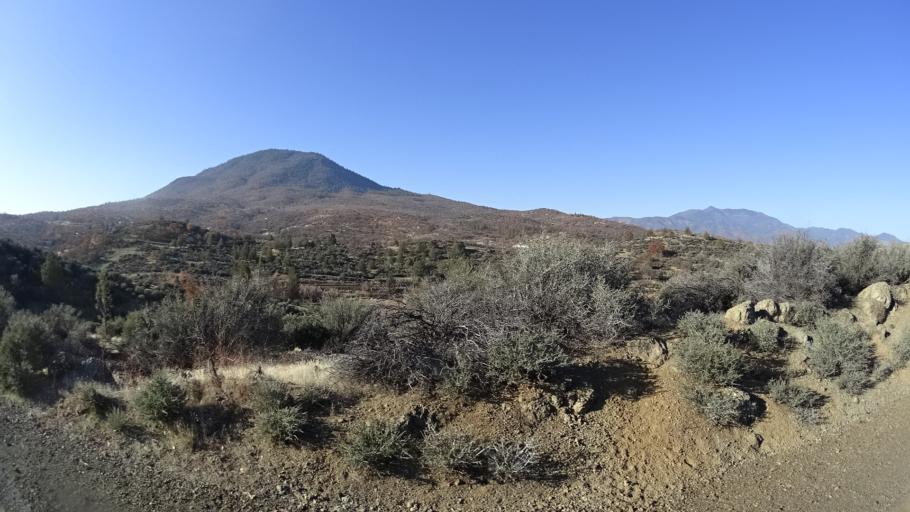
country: US
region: California
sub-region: Siskiyou County
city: Montague
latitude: 41.8941
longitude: -122.4859
